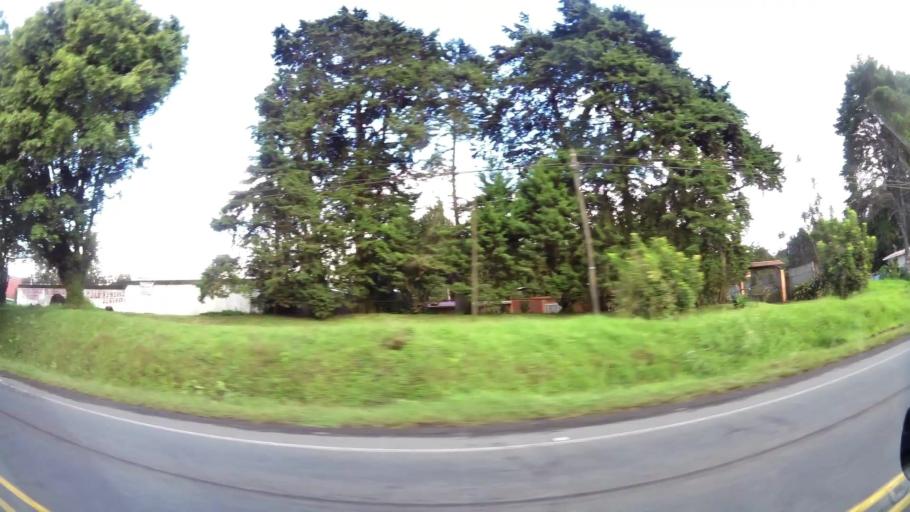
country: CR
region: Heredia
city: Angeles
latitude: 10.0286
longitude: -84.0213
